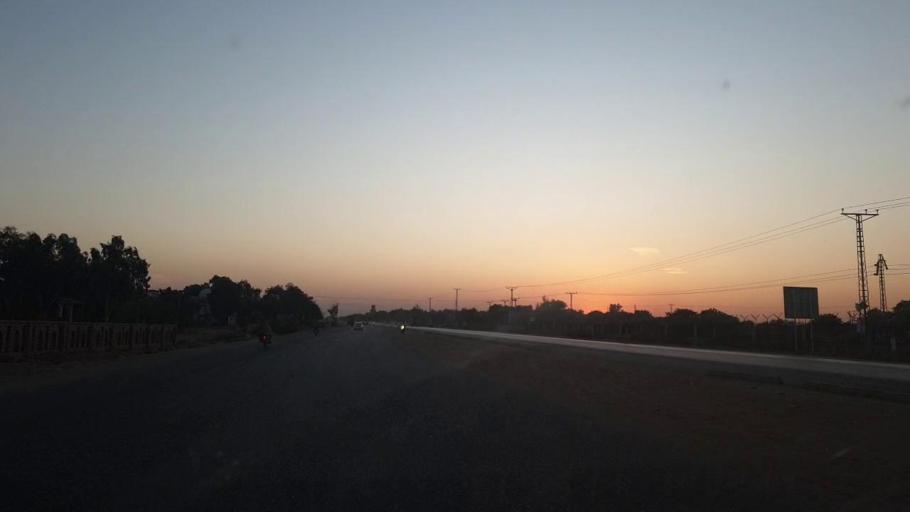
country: PK
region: Sindh
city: Jamshoro
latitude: 25.4178
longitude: 68.2769
